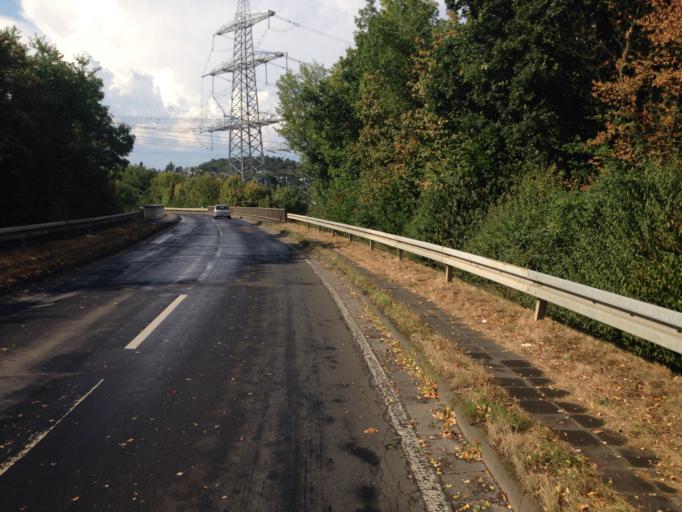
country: DE
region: Hesse
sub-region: Regierungsbezirk Giessen
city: Giessen
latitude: 50.6082
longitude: 8.6590
